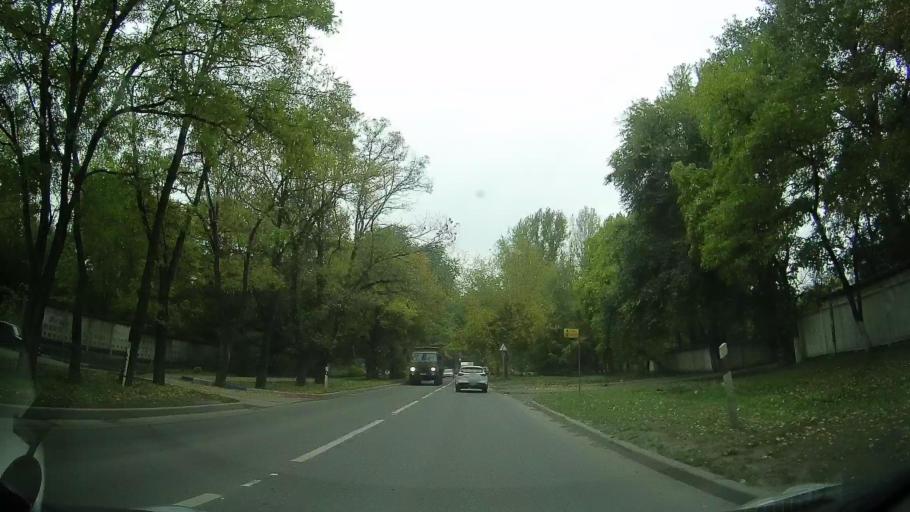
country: RU
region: Rostov
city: Severnyy
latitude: 47.2744
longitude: 39.6645
